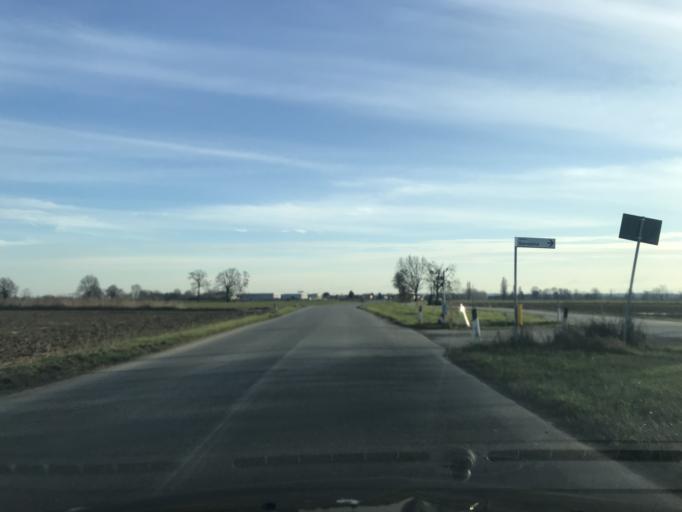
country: IT
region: Lombardy
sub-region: Provincia di Lodi
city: Bargano
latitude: 45.2499
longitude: 9.4370
